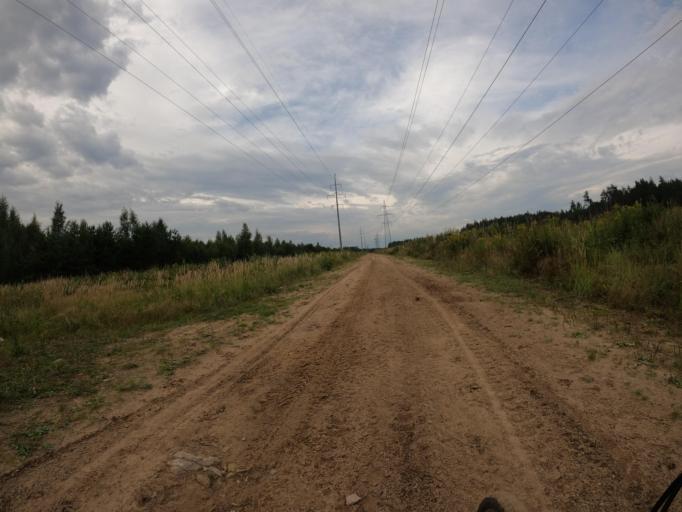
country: RU
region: Moskovskaya
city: Rodniki
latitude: 55.6732
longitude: 38.0826
